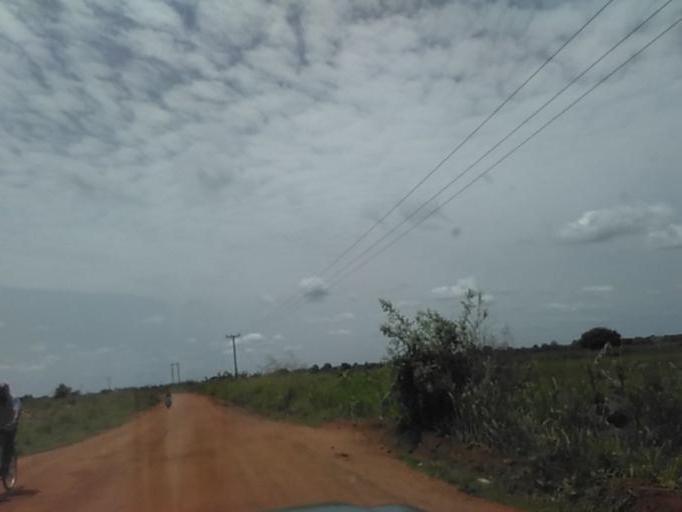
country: GH
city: Akropong
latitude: 6.0926
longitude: 0.2281
